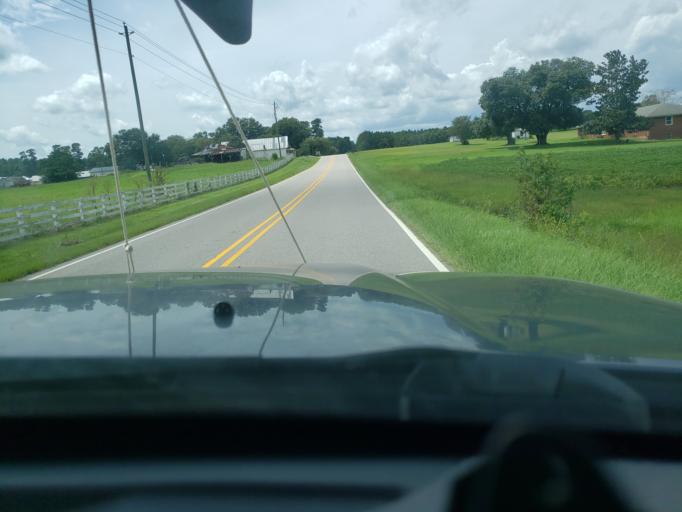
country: US
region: North Carolina
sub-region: Wake County
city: Rolesville
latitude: 35.8833
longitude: -78.4079
